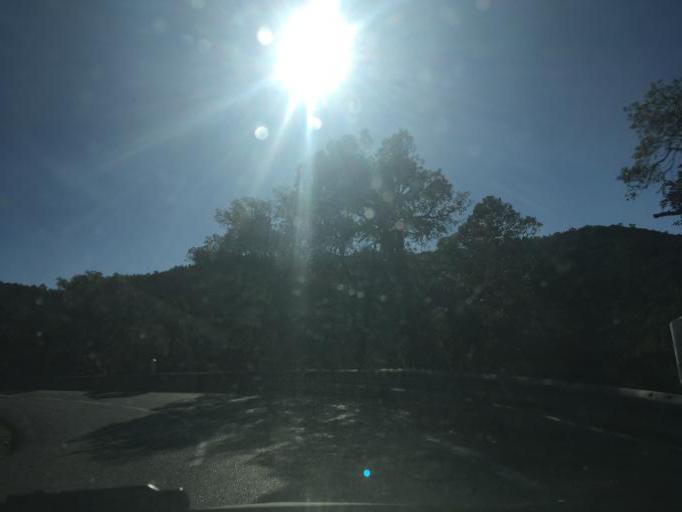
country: FR
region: Provence-Alpes-Cote d'Azur
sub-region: Departement du Var
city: La Garde-Freinet
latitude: 43.3306
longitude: 6.4484
